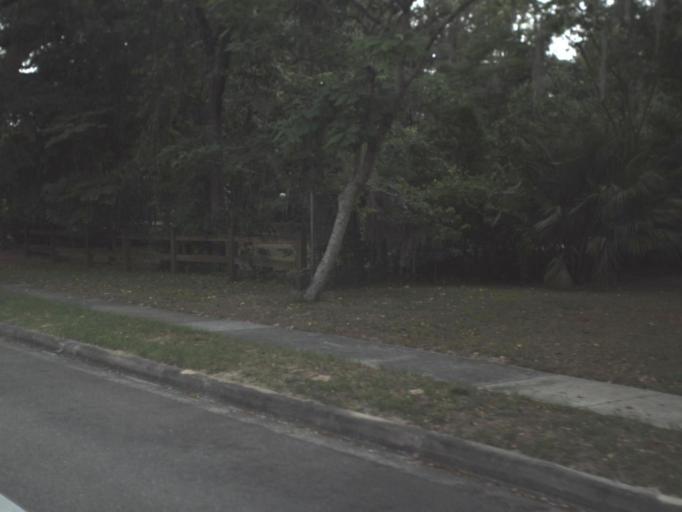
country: US
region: Florida
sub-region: Clay County
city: Keystone Heights
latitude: 29.7814
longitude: -82.0307
